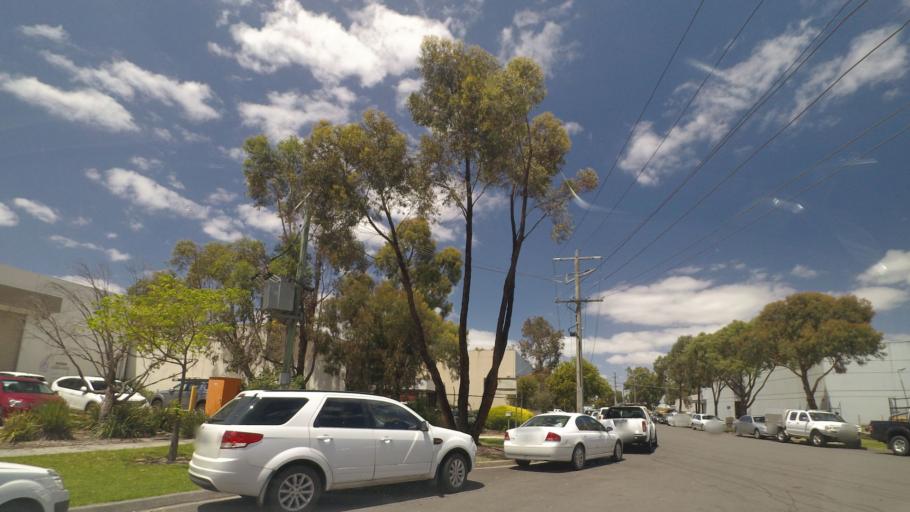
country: AU
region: Victoria
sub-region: Maroondah
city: Bayswater North
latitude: -37.8184
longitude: 145.2955
